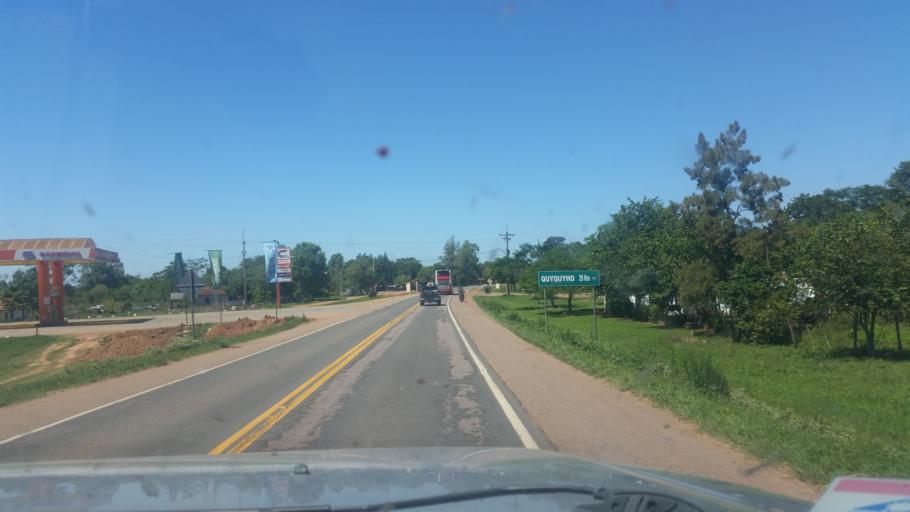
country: PY
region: Paraguari
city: Caapucu
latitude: -26.2382
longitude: -57.1755
